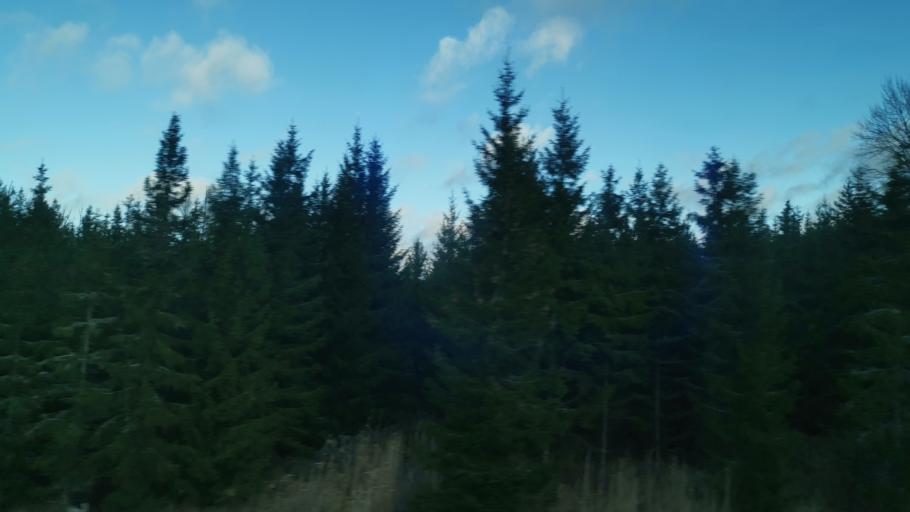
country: SE
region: Soedermanland
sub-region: Gnesta Kommun
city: Gnesta
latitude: 59.0685
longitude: 17.1351
